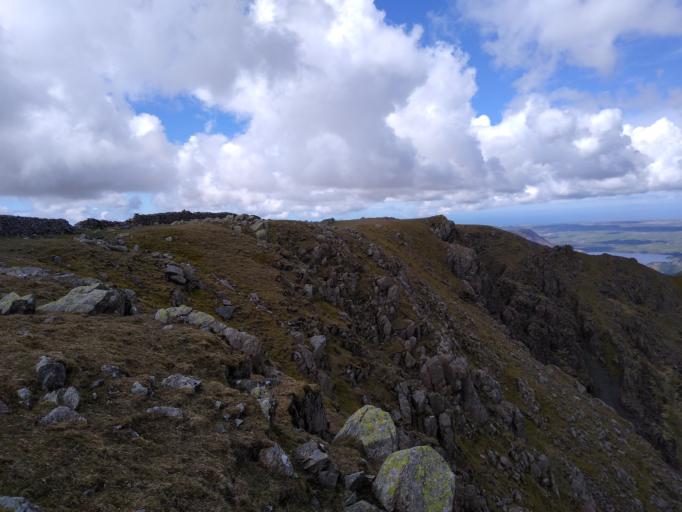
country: GB
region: England
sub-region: Cumbria
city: Cockermouth
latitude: 54.4910
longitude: -3.2982
